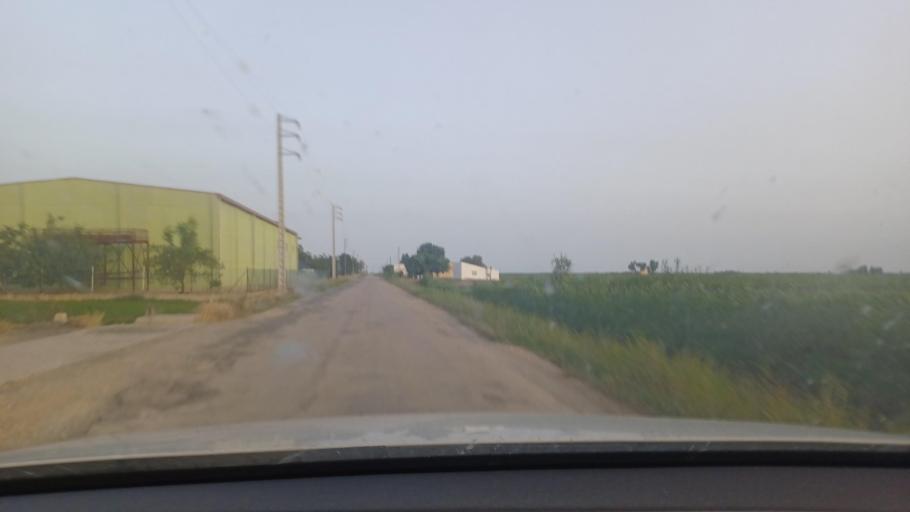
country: ES
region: Catalonia
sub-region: Provincia de Tarragona
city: Deltebre
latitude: 40.6737
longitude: 0.6611
